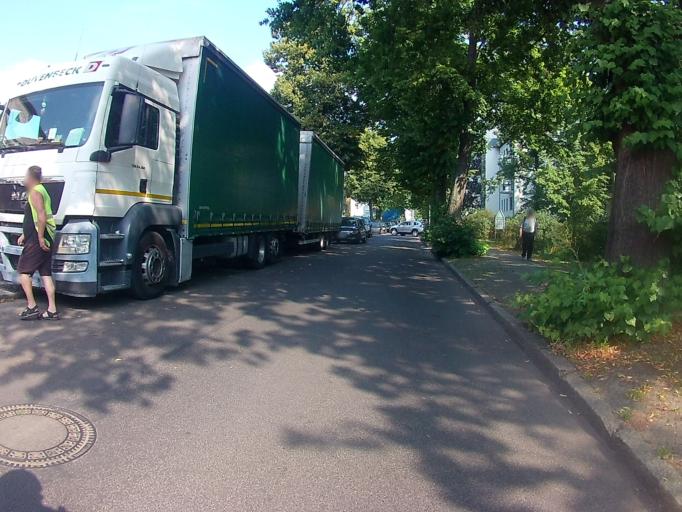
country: DE
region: Berlin
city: Grunau
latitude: 52.4154
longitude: 13.5823
